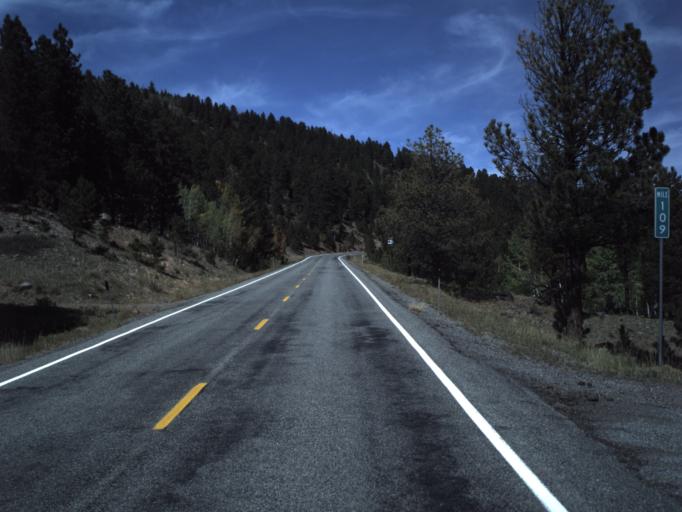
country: US
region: Utah
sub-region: Wayne County
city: Loa
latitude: 38.1349
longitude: -111.3280
